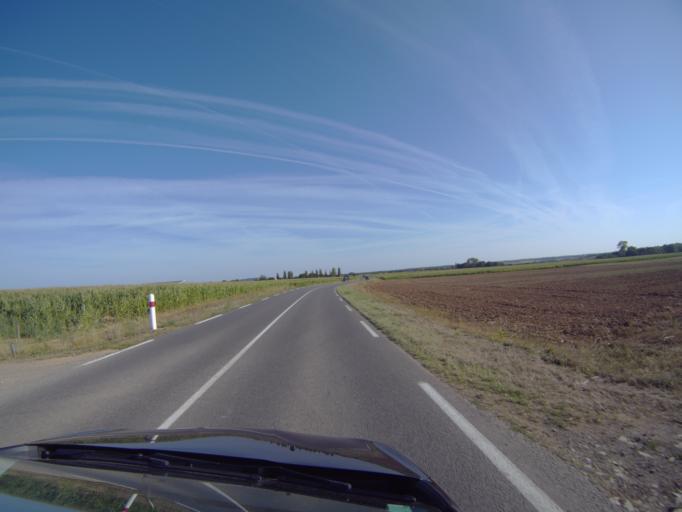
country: FR
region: Pays de la Loire
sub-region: Departement de la Vendee
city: Jard-sur-Mer
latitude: 46.4375
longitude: -1.5785
